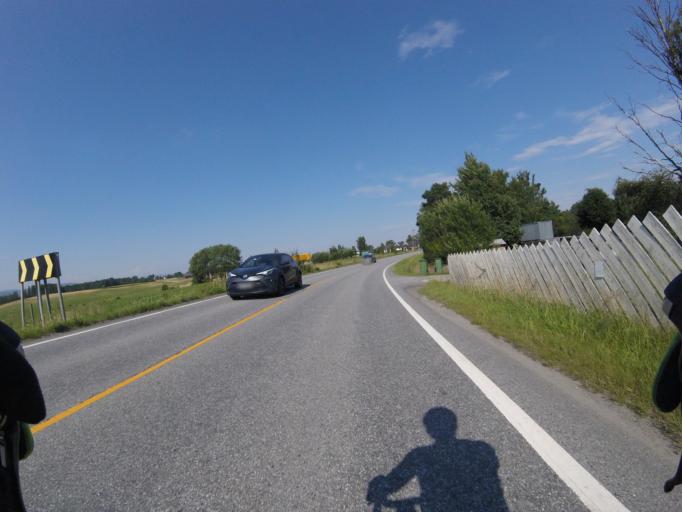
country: NO
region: Akershus
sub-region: Sorum
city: Frogner
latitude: 60.0421
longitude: 11.1139
